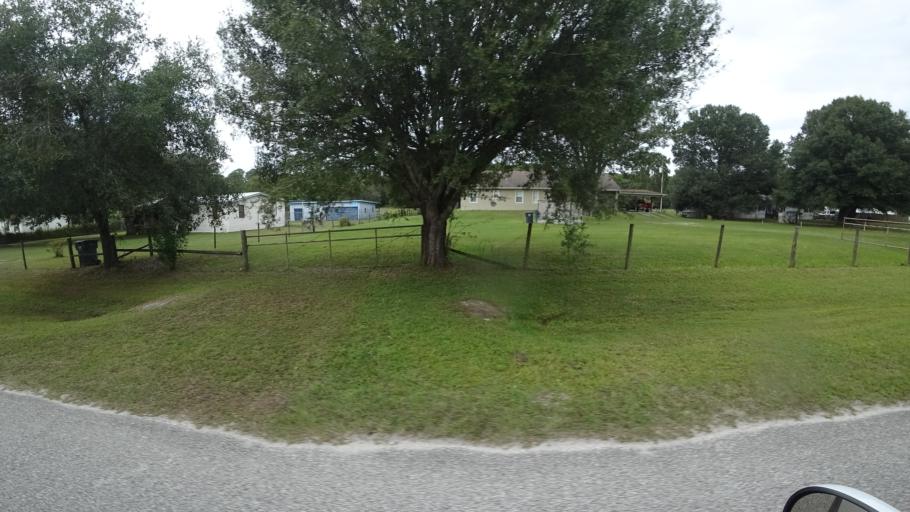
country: US
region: Florida
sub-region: Hillsborough County
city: Sun City Center
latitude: 27.6631
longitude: -82.3387
